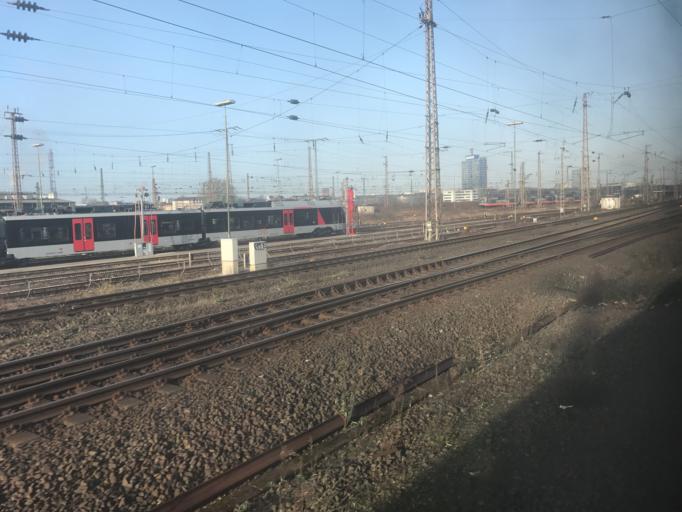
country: DE
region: North Rhine-Westphalia
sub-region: Regierungsbezirk Dusseldorf
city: Duisburg
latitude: 51.4233
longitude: 6.7767
